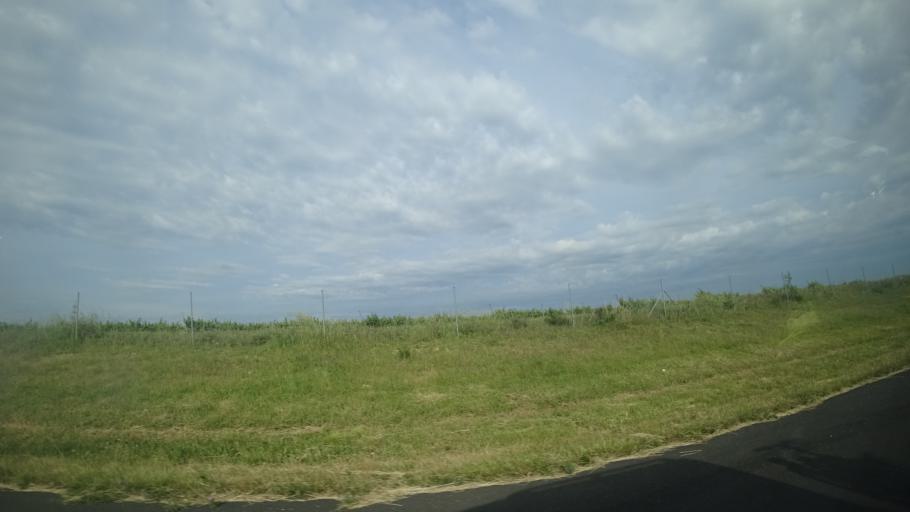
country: FR
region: Languedoc-Roussillon
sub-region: Departement de l'Herault
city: Aspiran
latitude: 43.5930
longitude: 3.4655
